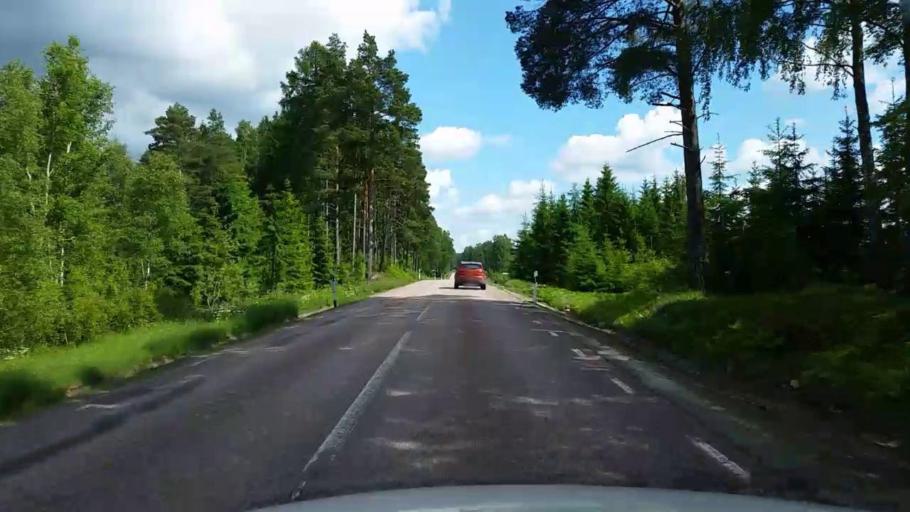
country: SE
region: Vaestmanland
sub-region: Skinnskattebergs Kommun
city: Skinnskatteberg
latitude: 59.7538
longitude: 15.8152
